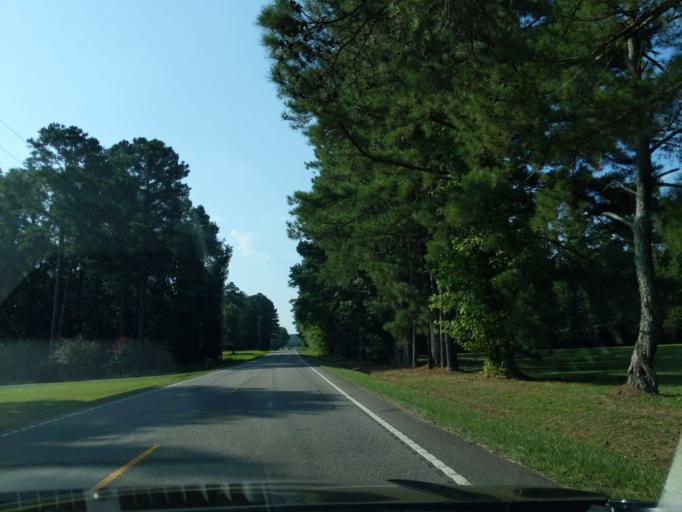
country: US
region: South Carolina
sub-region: Lexington County
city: Leesville
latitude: 34.0563
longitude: -81.5571
